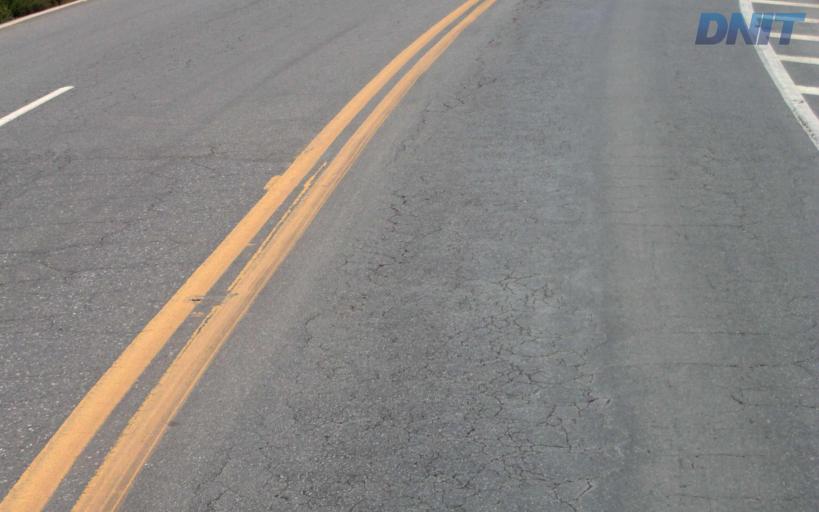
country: BR
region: Minas Gerais
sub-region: Nova Era
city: Nova Era
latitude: -19.7236
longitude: -43.0091
